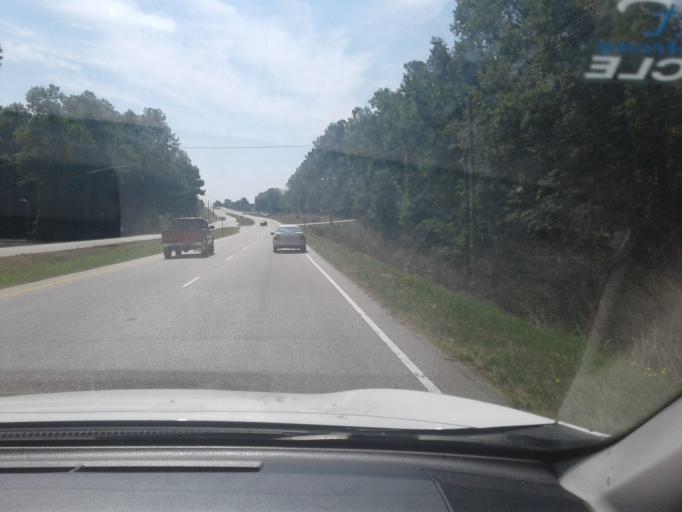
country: US
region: North Carolina
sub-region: Harnett County
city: Erwin
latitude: 35.3344
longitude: -78.6724
